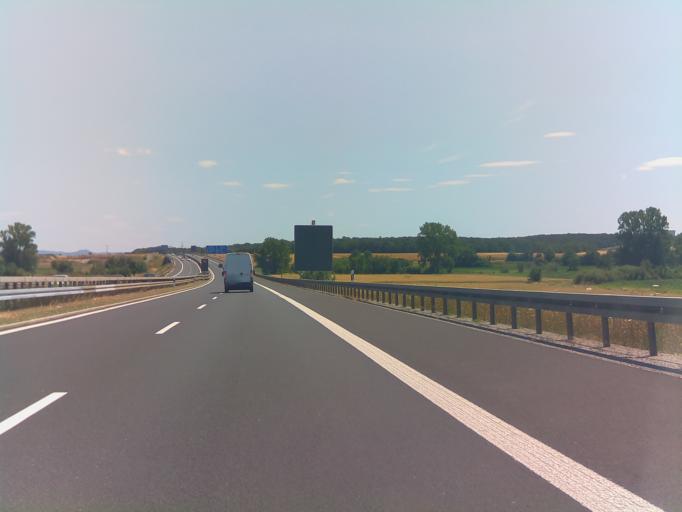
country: DE
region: Bavaria
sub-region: Regierungsbezirk Unterfranken
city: Geldersheim
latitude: 50.0283
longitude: 10.1443
